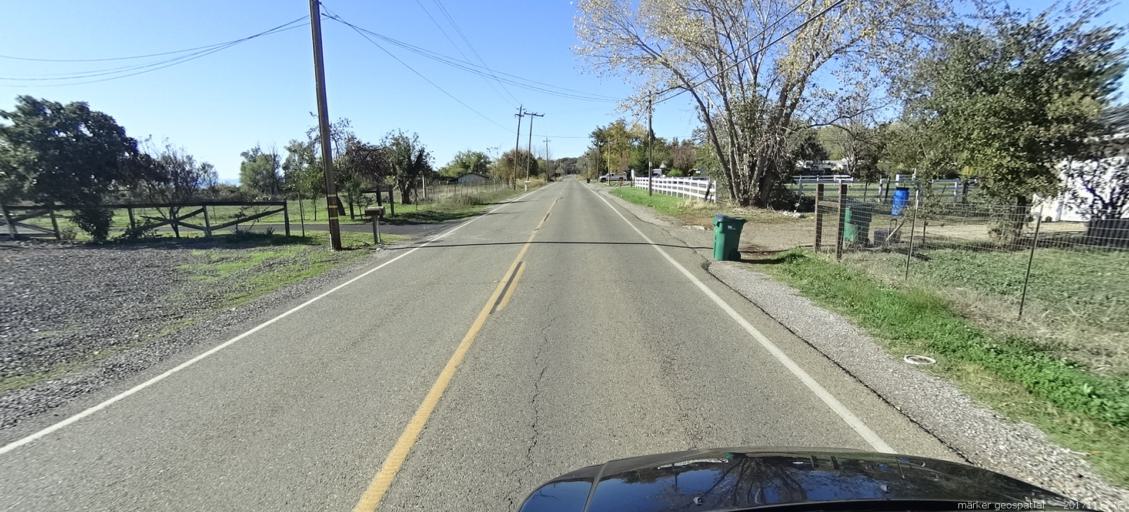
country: US
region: California
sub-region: Shasta County
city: Cottonwood
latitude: 40.4040
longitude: -122.2346
